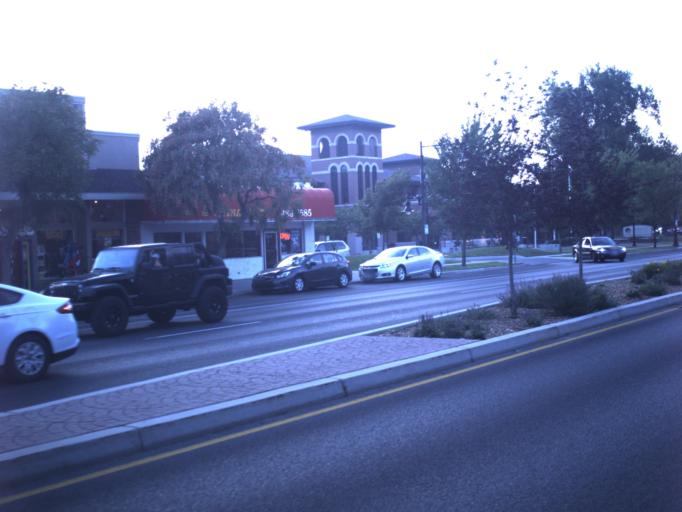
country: US
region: Utah
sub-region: Utah County
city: Springville
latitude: 40.1643
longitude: -111.6106
